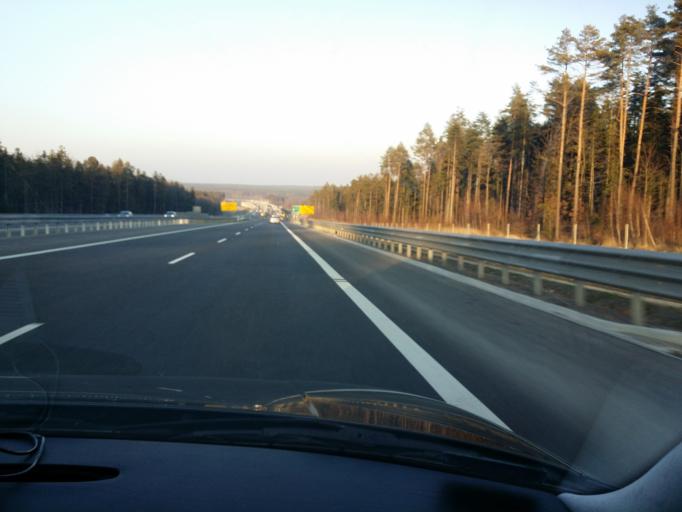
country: PL
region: Swietokrzyskie
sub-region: Powiat skarzyski
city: Skarzysko-Kamienna
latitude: 51.1495
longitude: 20.8405
